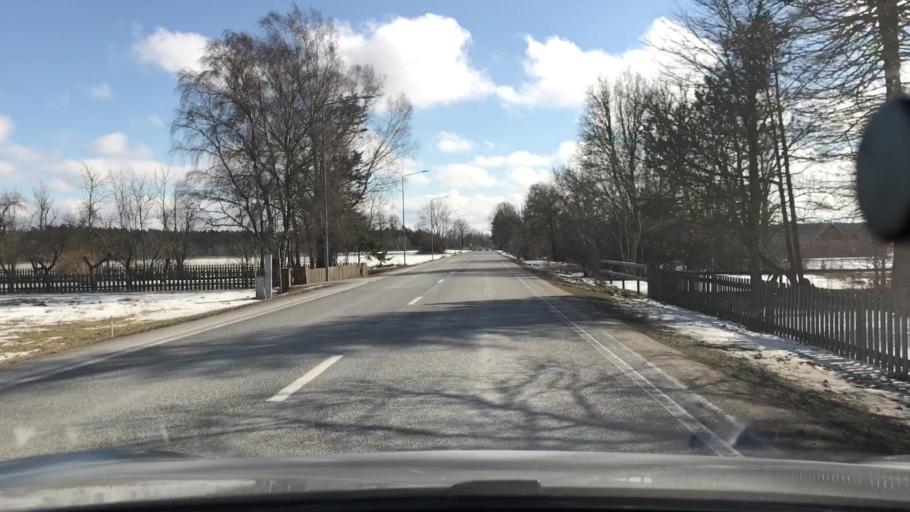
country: SE
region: Gotland
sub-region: Gotland
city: Visby
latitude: 57.5263
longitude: 18.4405
